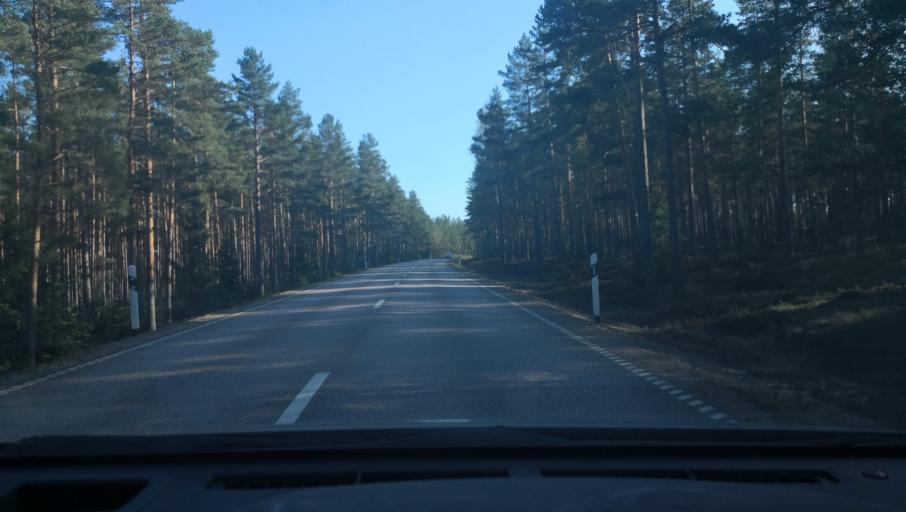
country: SE
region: Uppsala
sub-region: Heby Kommun
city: Tarnsjo
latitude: 60.1084
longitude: 16.8855
